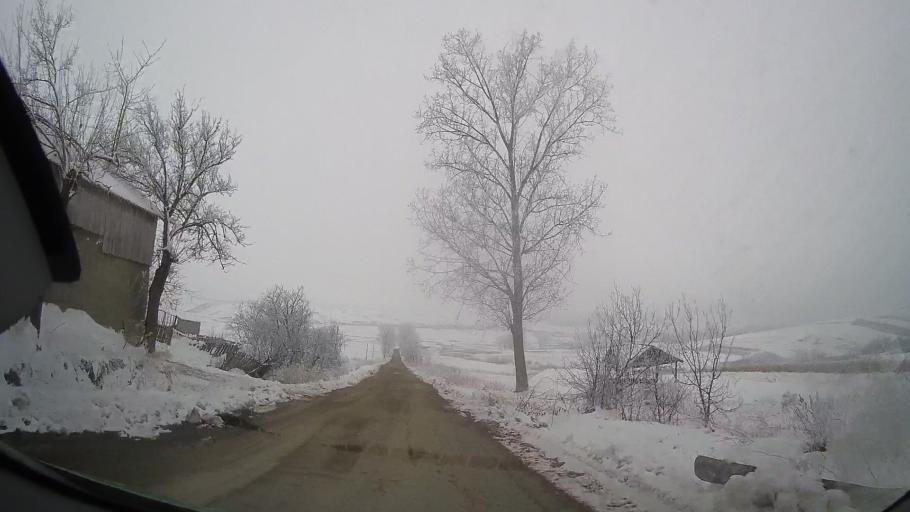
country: RO
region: Iasi
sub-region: Comuna Tansa
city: Tansa
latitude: 46.9139
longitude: 27.2222
